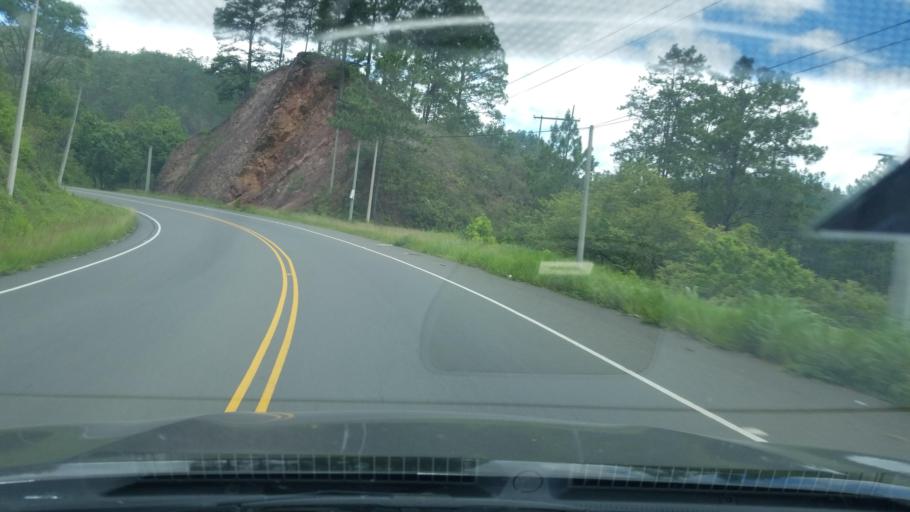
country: HN
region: Francisco Morazan
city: Talanga
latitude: 14.3648
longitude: -87.1427
